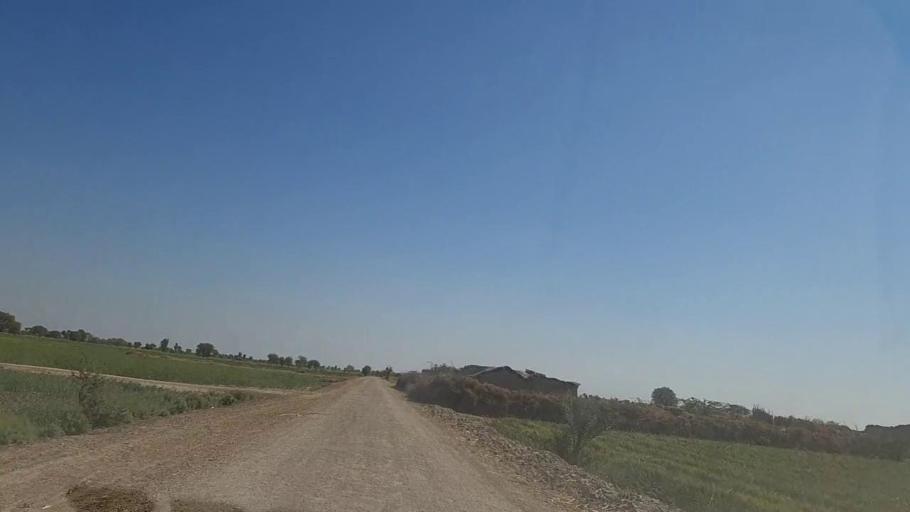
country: PK
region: Sindh
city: Digri
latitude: 25.1087
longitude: 69.1205
